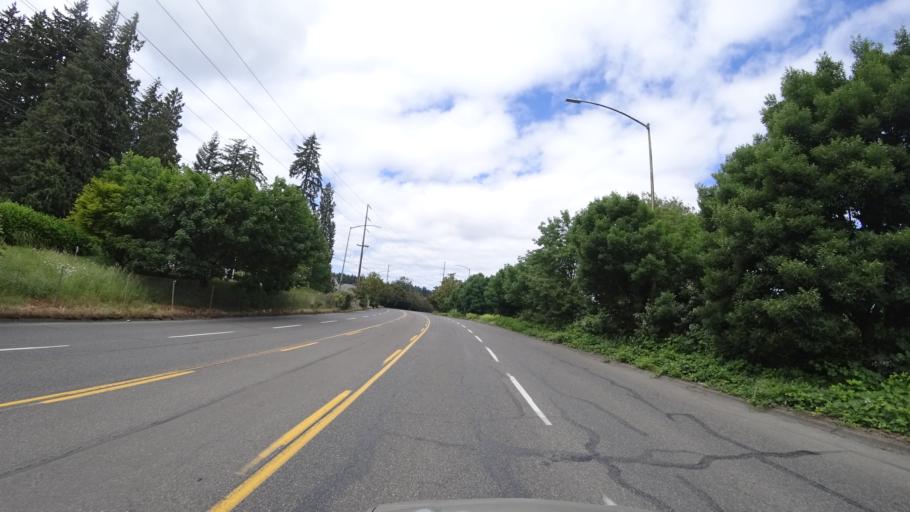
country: US
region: Oregon
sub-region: Washington County
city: West Haven
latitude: 45.6012
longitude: -122.7435
